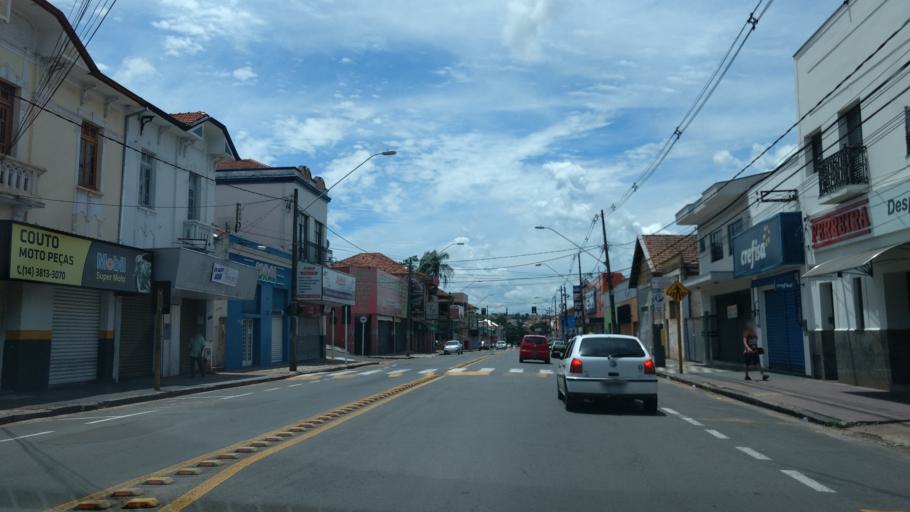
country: BR
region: Sao Paulo
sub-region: Botucatu
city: Botucatu
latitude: -22.8814
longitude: -48.4414
